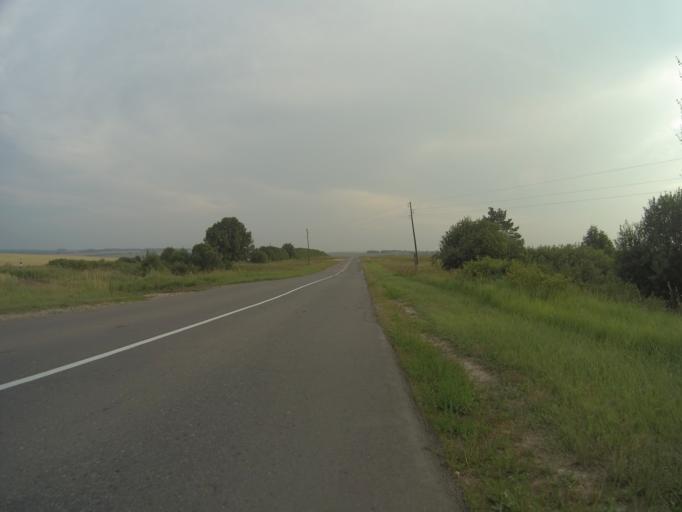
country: RU
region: Ivanovo
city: Gavrilov Posad
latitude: 56.3600
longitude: 40.2270
